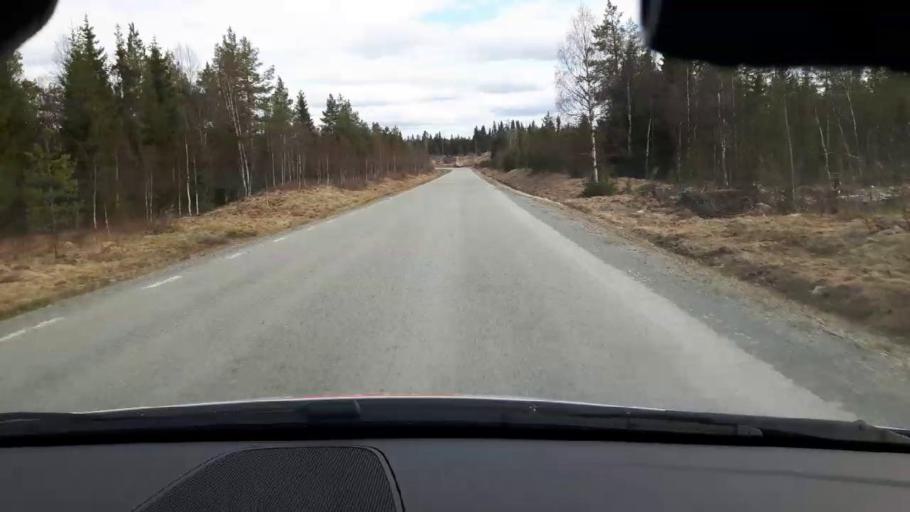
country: SE
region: Jaemtland
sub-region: Bergs Kommun
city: Hoverberg
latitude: 62.6882
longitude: 14.6344
